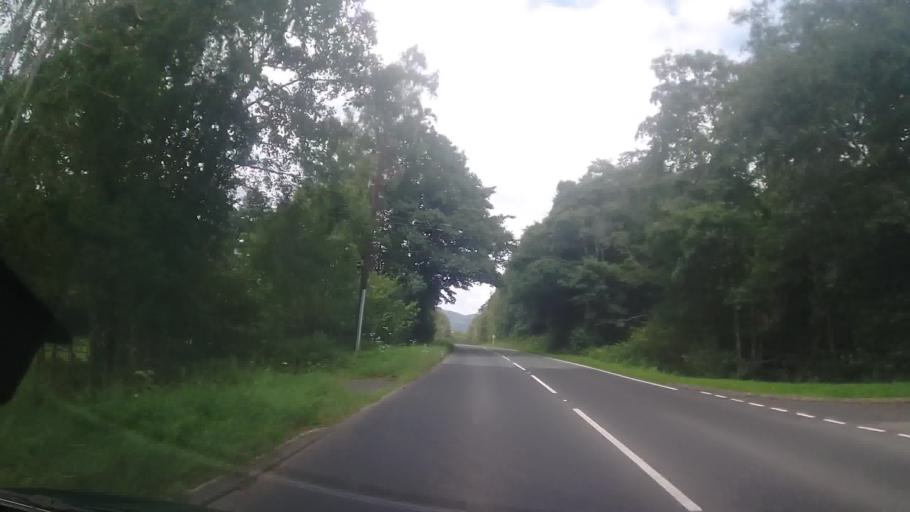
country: GB
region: Wales
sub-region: Gwynedd
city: Barmouth
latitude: 52.7272
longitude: -3.9831
